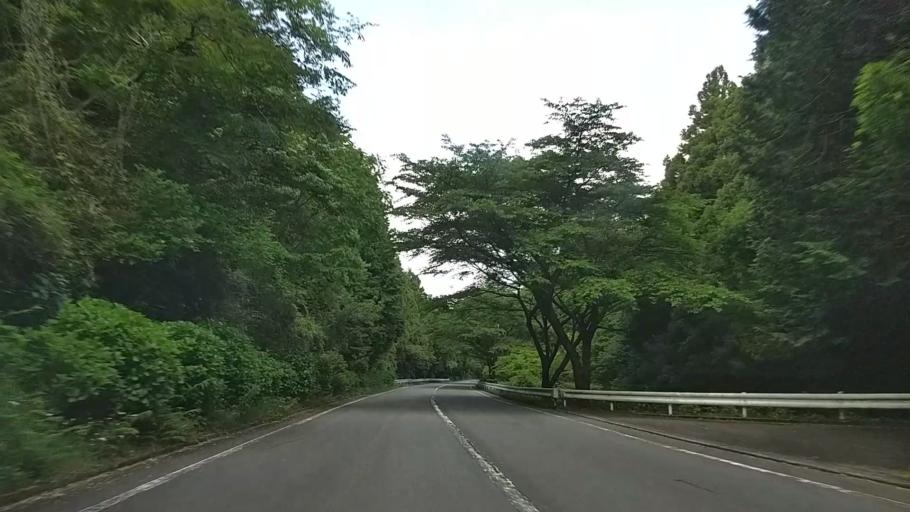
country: JP
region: Kanagawa
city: Odawara
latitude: 35.2258
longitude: 139.1174
